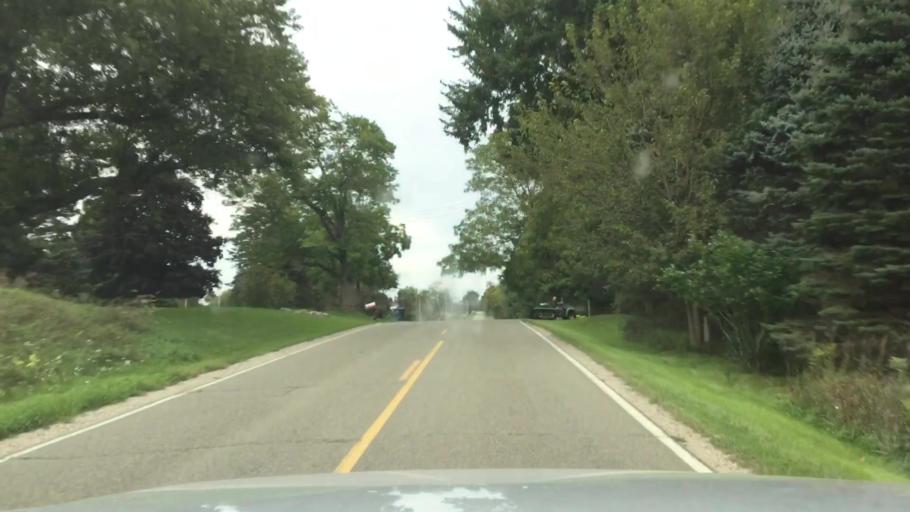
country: US
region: Michigan
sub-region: Shiawassee County
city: Durand
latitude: 42.8229
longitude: -83.9974
